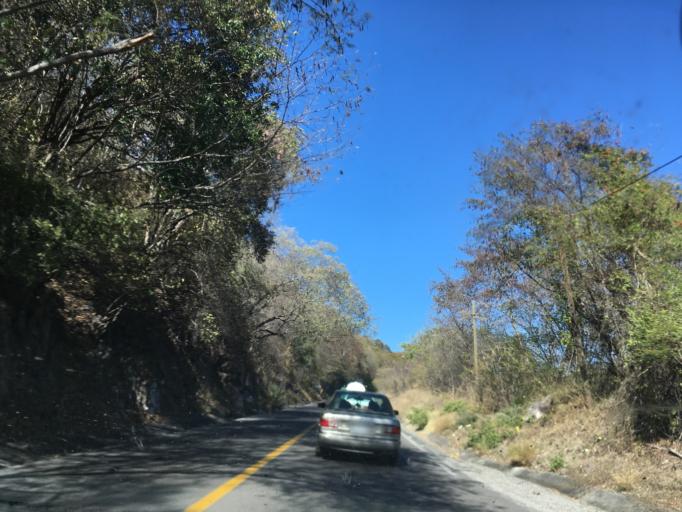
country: MX
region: Michoacan
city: Nueva Italia de Ruiz
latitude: 19.0812
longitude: -102.0633
